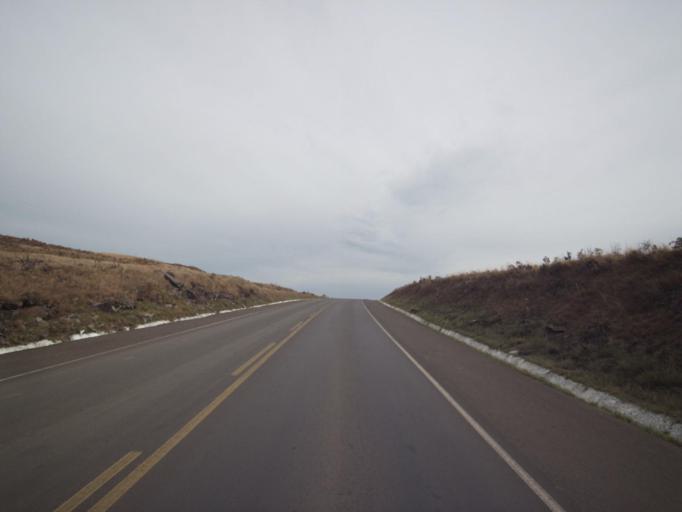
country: BR
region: Parana
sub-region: Palmas
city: Palmas
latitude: -26.7642
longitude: -51.6688
